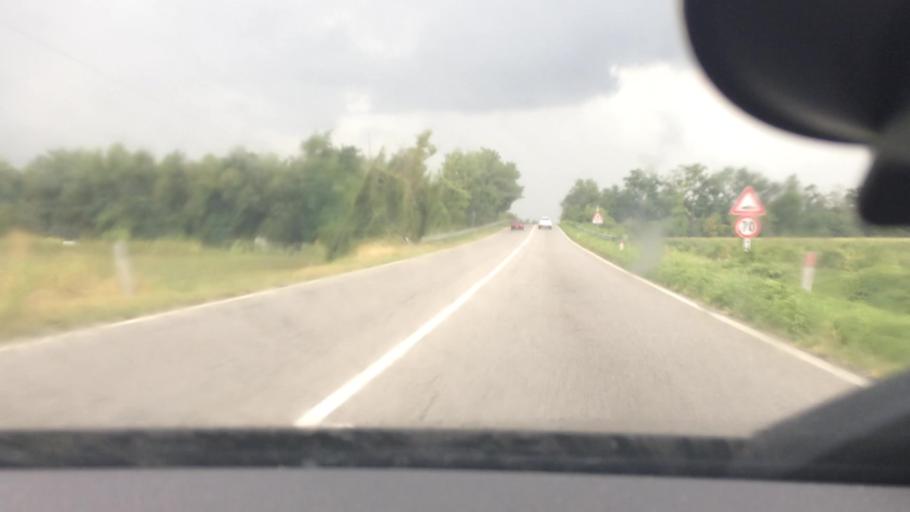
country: IT
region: Lombardy
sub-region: Citta metropolitana di Milano
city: Nerviano
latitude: 45.5623
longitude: 8.9927
